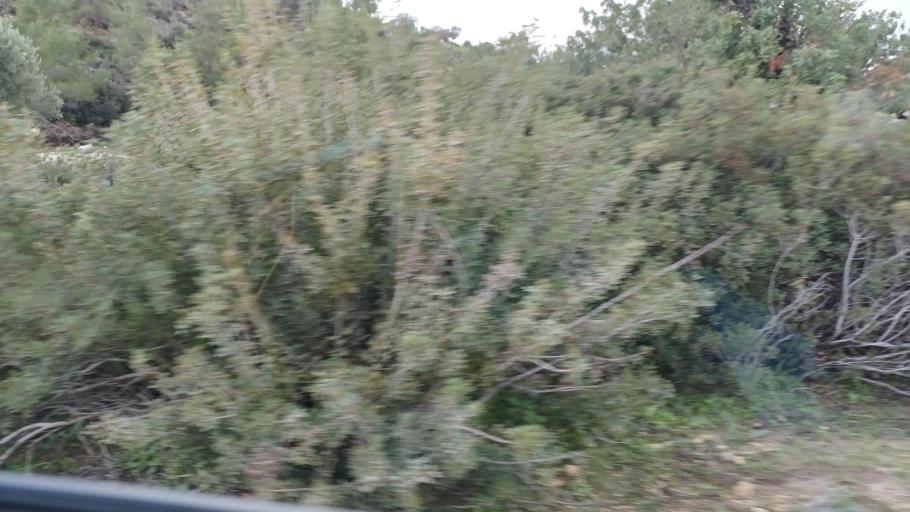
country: CY
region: Limassol
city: Sotira
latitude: 34.7034
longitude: 32.8642
